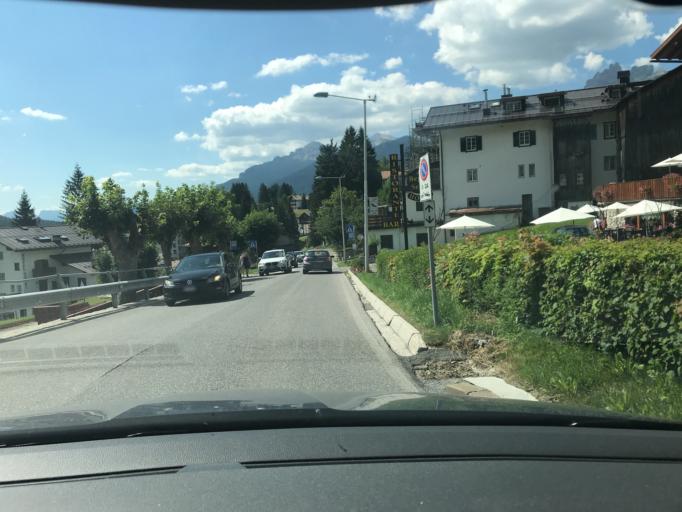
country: IT
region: Veneto
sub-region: Provincia di Belluno
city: Cortina d'Ampezzo
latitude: 46.5423
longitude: 12.1290
